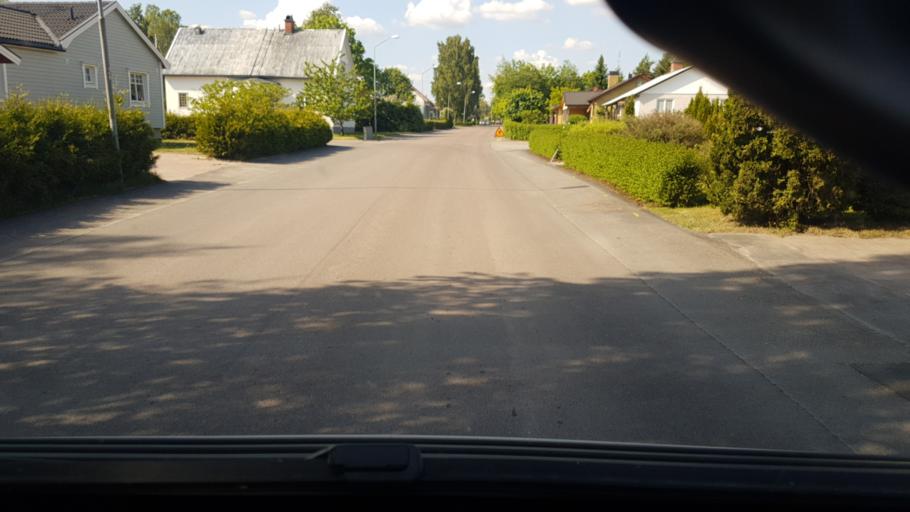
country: SE
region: Vaermland
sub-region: Eda Kommun
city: Charlottenberg
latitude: 59.8874
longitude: 12.3066
